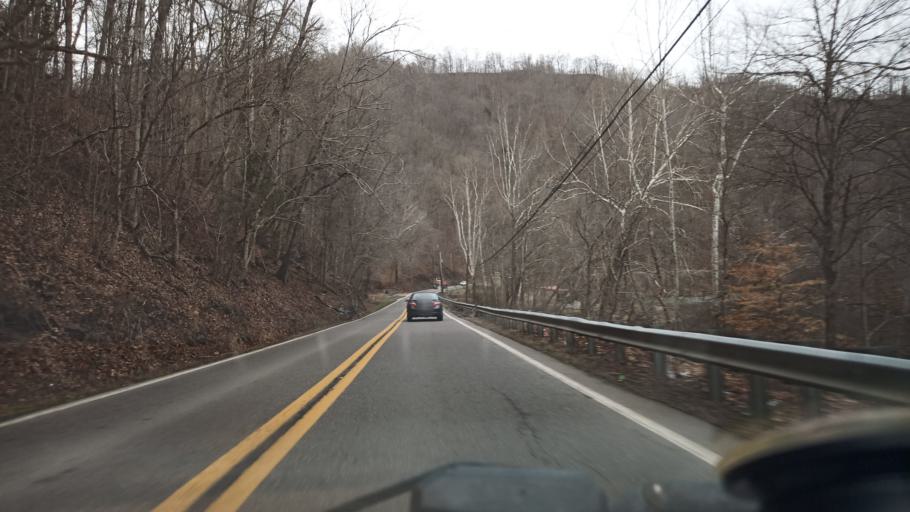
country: US
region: West Virginia
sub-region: Logan County
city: Mallory
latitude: 37.6621
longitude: -81.8654
